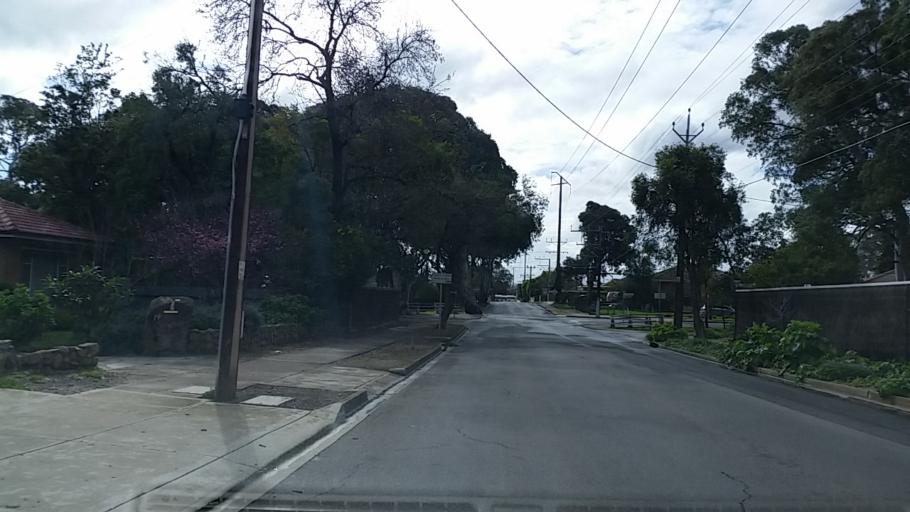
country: AU
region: South Australia
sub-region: Campbelltown
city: Campbelltown
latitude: -34.8916
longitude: 138.6814
